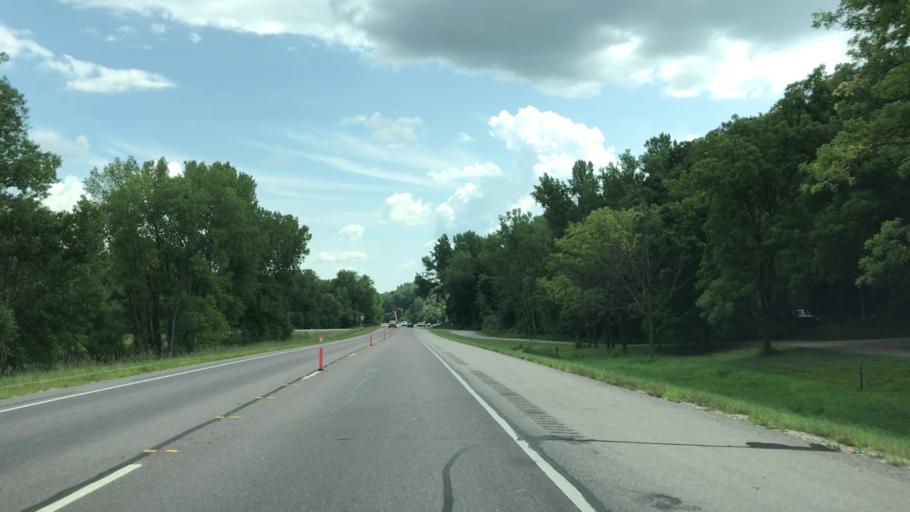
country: US
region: Minnesota
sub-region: Nicollet County
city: Saint Peter
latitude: 44.3718
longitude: -93.9666
